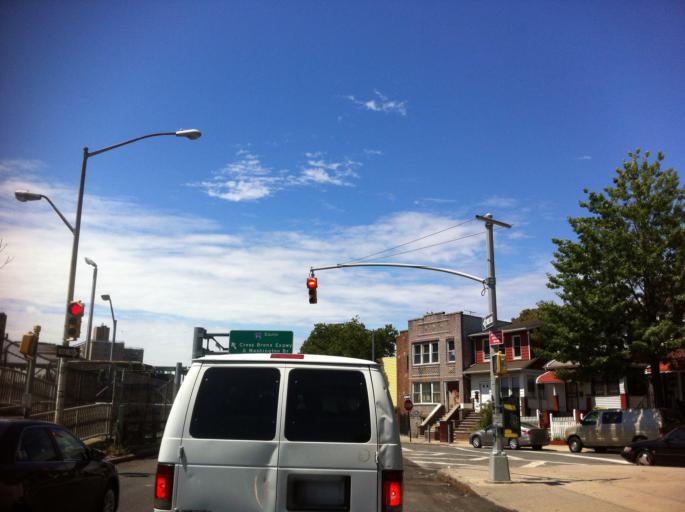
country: US
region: New York
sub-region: Bronx
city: The Bronx
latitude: 40.8318
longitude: -73.8549
